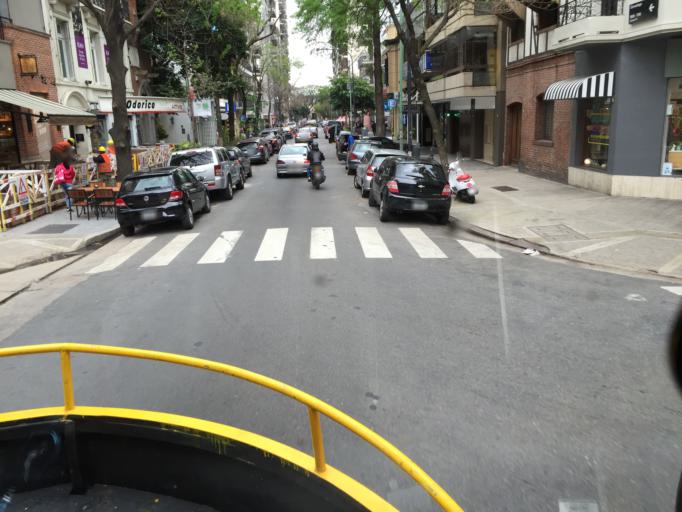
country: AR
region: Buenos Aires F.D.
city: Colegiales
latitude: -34.5663
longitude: -58.4371
